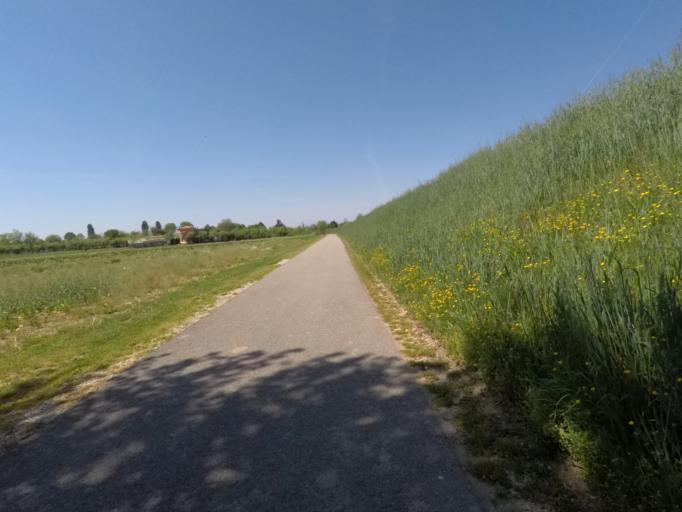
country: IT
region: Veneto
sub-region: Provincia di Treviso
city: Oderzo
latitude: 45.7868
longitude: 12.5117
